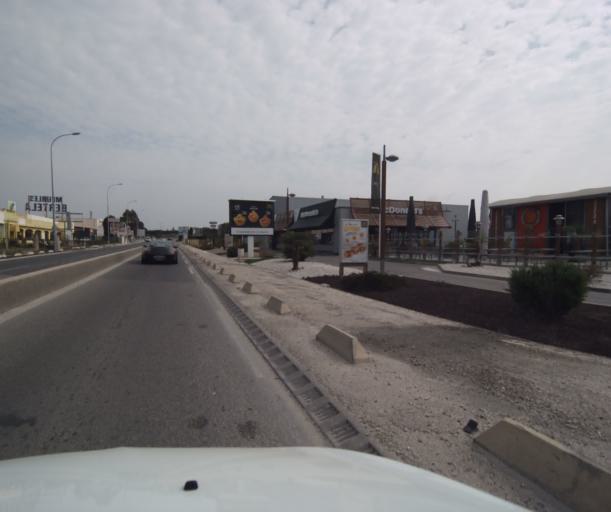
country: FR
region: Provence-Alpes-Cote d'Azur
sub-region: Departement du Var
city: La Farlede
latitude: 43.1391
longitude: 6.0340
